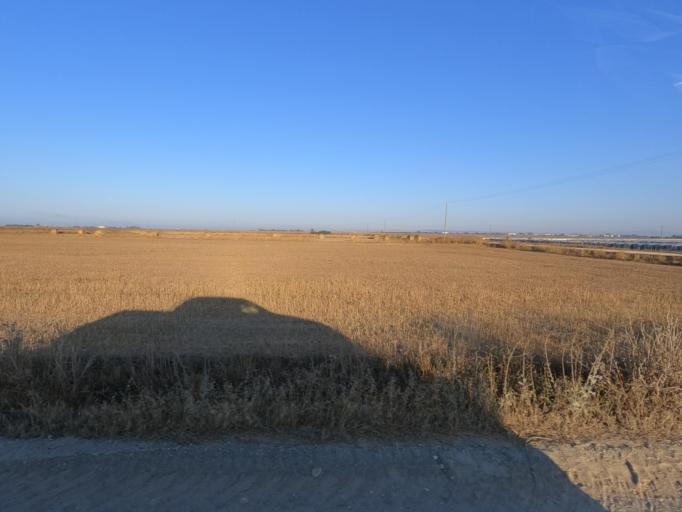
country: CY
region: Ammochostos
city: Avgorou
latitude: 35.0141
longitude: 33.8026
